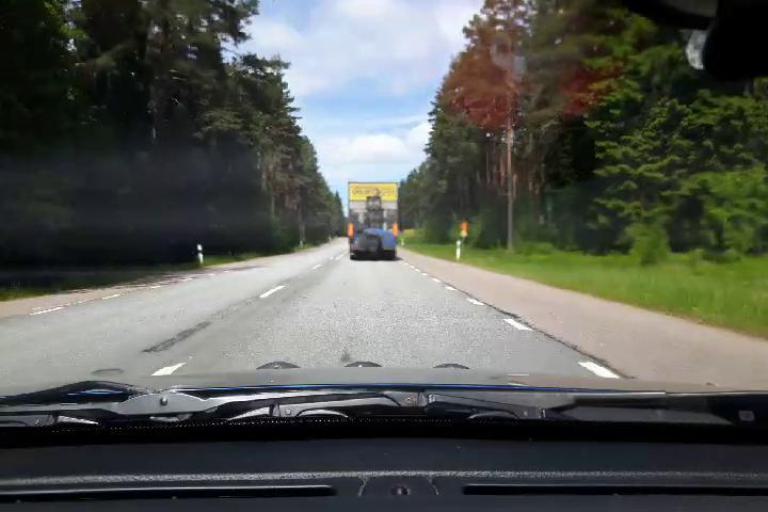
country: SE
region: Uppsala
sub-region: Tierps Kommun
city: Tierp
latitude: 60.2018
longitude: 17.4819
